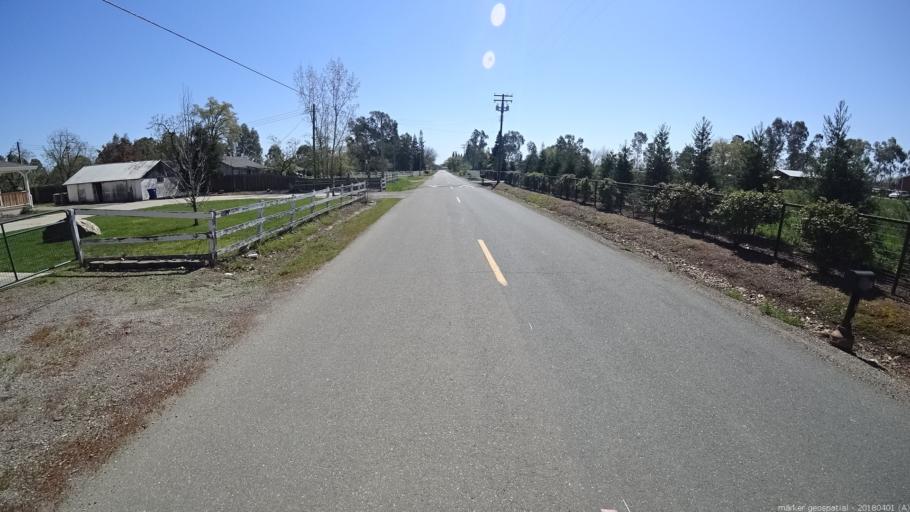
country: US
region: California
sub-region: Sacramento County
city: Wilton
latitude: 38.4073
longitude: -121.2561
